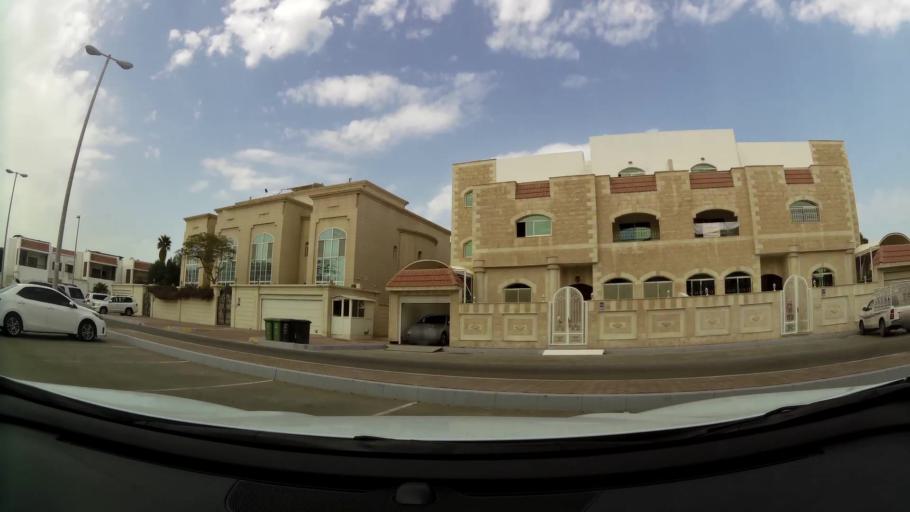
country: AE
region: Abu Dhabi
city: Abu Dhabi
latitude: 24.4505
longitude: 54.3602
